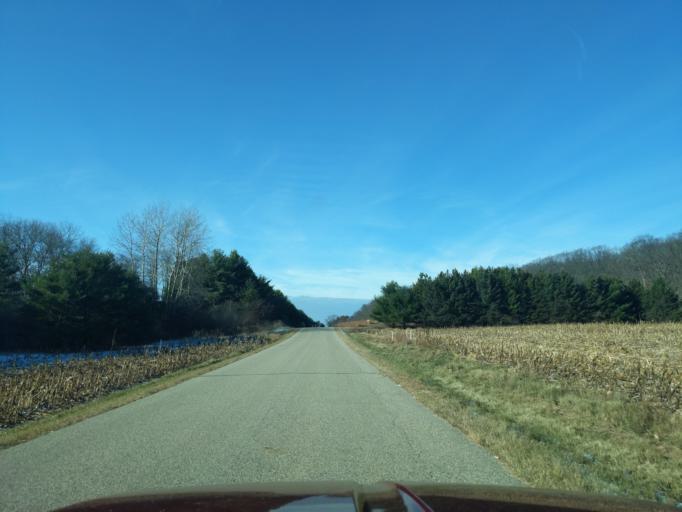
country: US
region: Wisconsin
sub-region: Waushara County
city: Silver Lake
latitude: 44.1133
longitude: -89.1777
